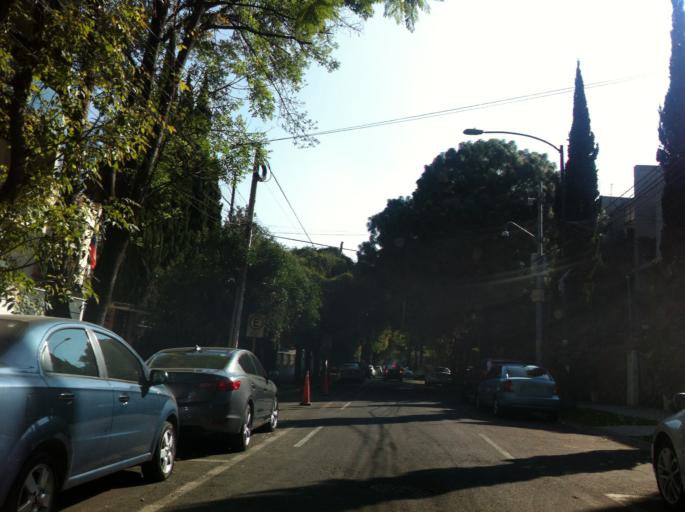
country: MX
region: Mexico City
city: Miguel Hidalgo
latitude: 19.4354
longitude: -99.1948
